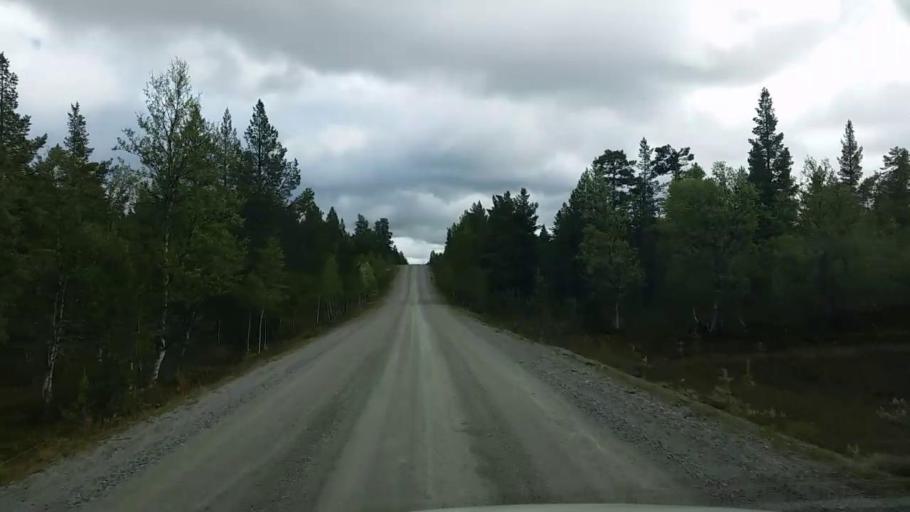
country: NO
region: Hedmark
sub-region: Engerdal
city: Engerdal
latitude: 62.3418
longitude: 12.6090
